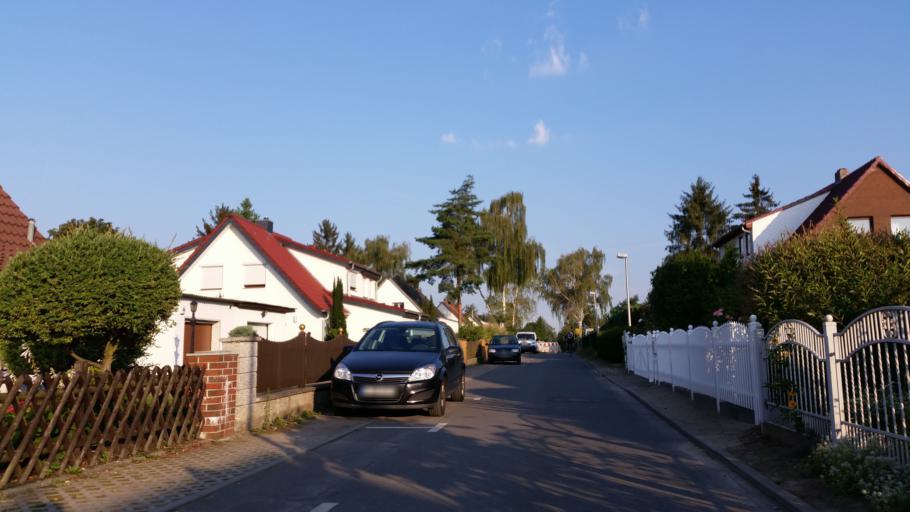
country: DE
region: Berlin
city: Marienfelde
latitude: 52.3998
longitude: 13.3580
